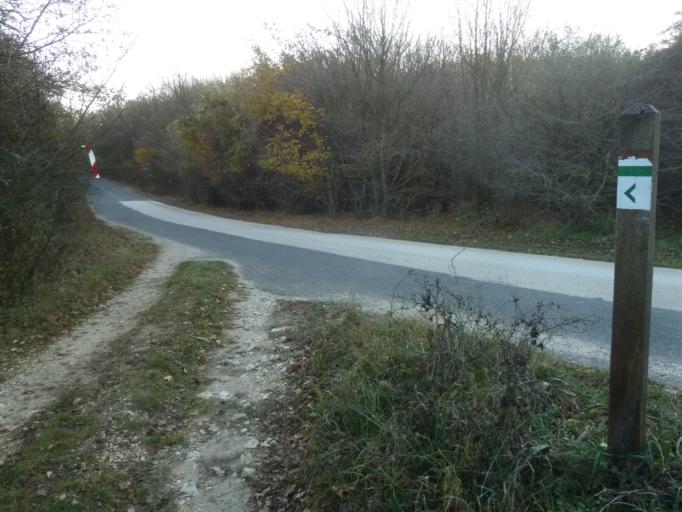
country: HU
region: Fejer
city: Zamoly
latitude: 47.3629
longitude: 18.3513
